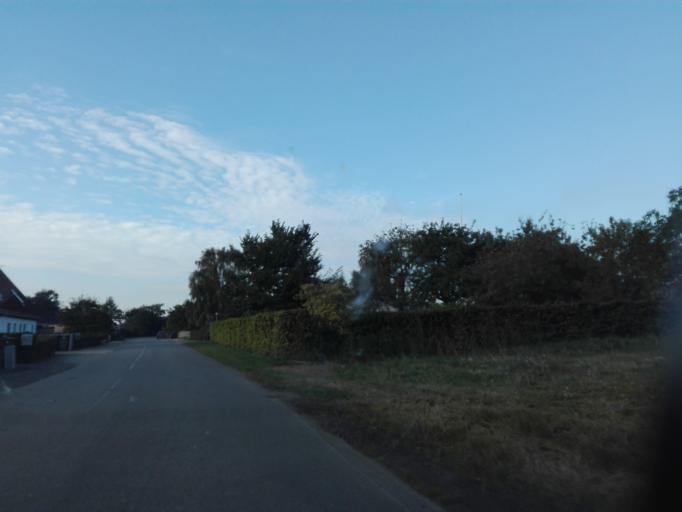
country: DK
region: Central Jutland
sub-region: Odder Kommune
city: Odder
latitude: 55.9553
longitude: 10.1902
